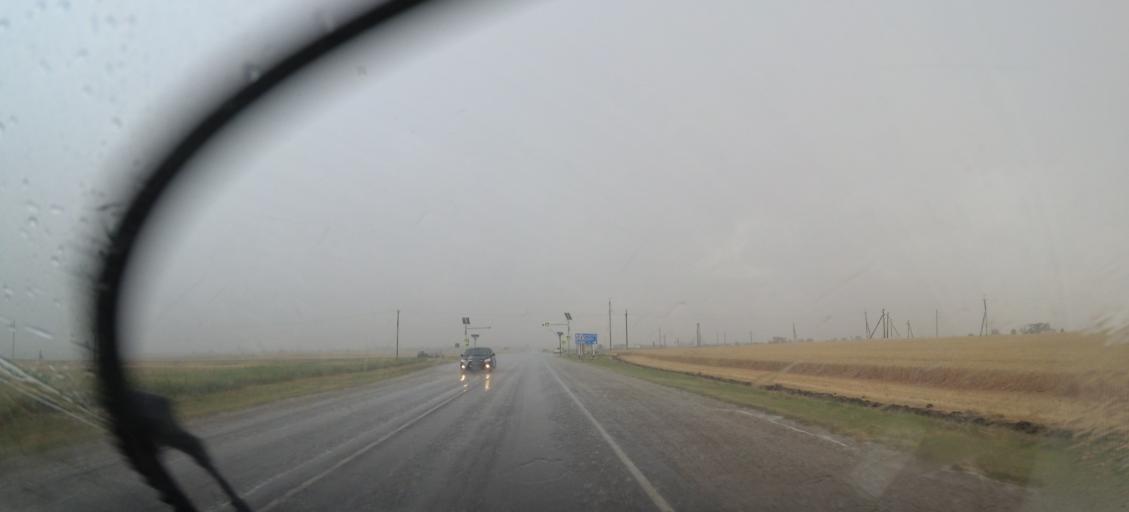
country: RU
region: Rostov
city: Proletarsk
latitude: 46.6768
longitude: 41.7031
